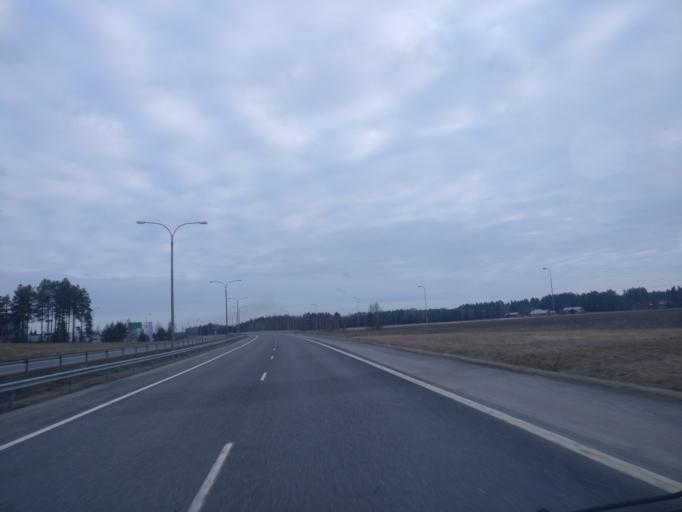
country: FI
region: Northern Ostrobothnia
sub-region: Oulu
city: Kempele
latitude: 64.9063
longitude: 25.5362
